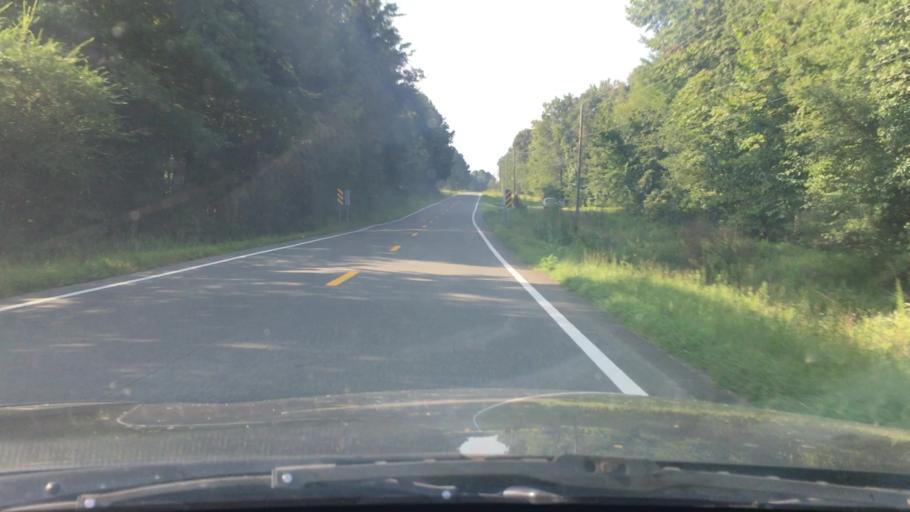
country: US
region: North Carolina
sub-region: Alamance County
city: Green Level
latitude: 36.2206
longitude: -79.3223
